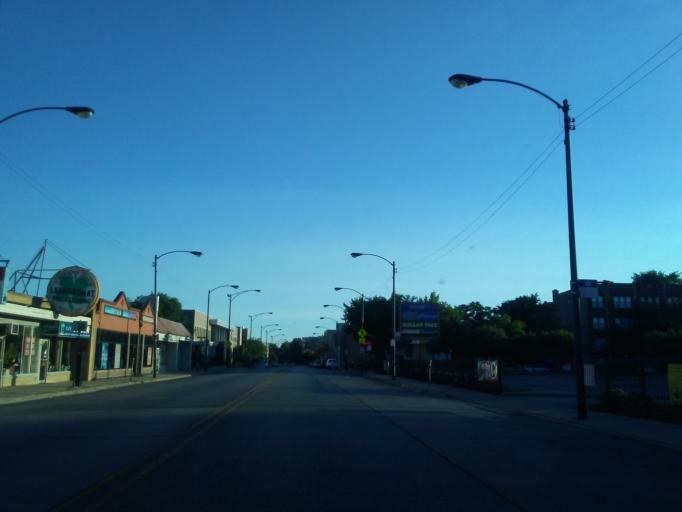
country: US
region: Illinois
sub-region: Cook County
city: Lincolnwood
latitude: 41.9788
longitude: -87.6926
